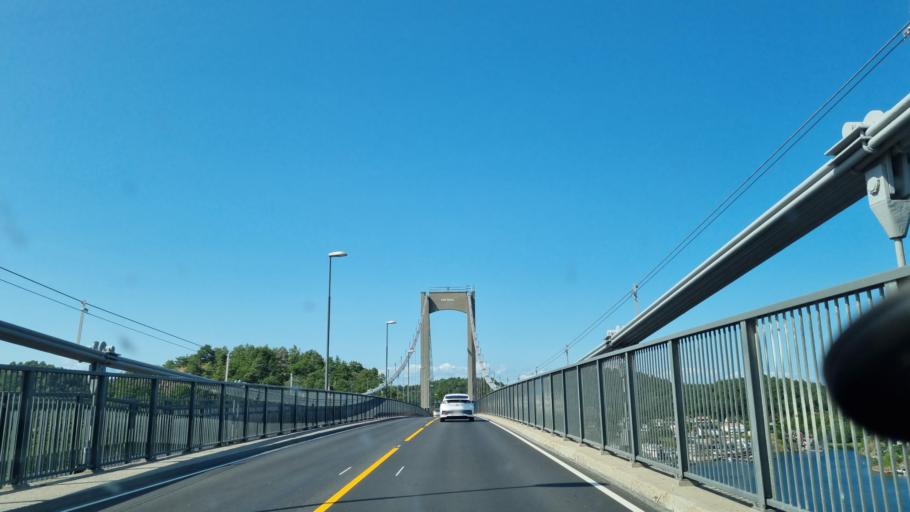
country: NO
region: Aust-Agder
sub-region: Arendal
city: Arendal
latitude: 58.4708
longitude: 8.8230
